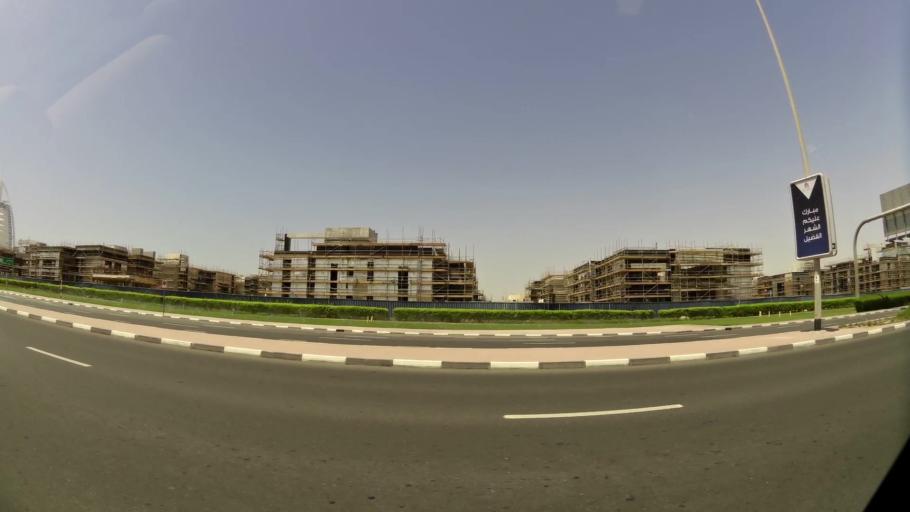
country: AE
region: Dubai
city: Dubai
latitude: 25.1309
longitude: 55.1907
